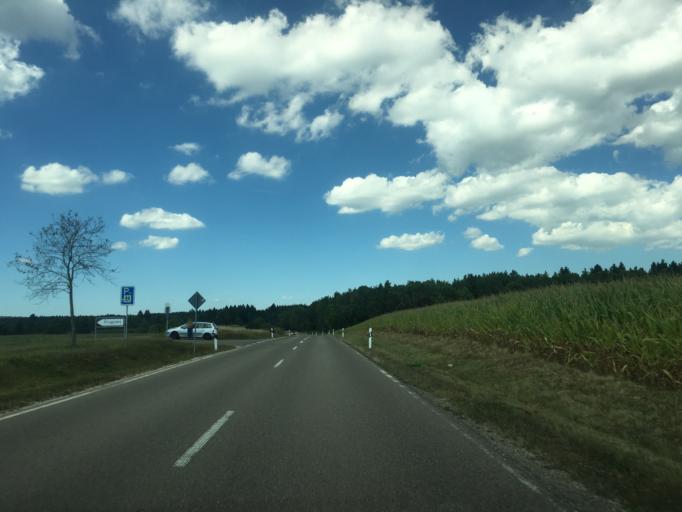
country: DE
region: Baden-Wuerttemberg
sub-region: Tuebingen Region
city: Hayingen
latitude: 48.2881
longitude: 9.4659
